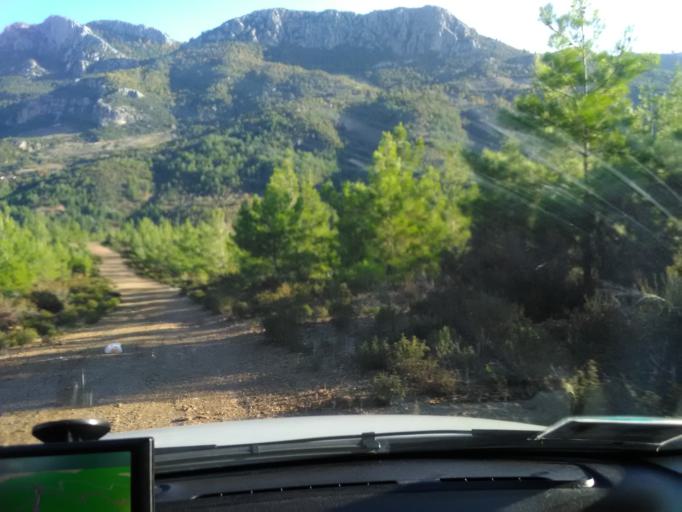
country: TR
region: Antalya
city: Gazipasa
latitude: 36.3084
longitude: 32.3955
